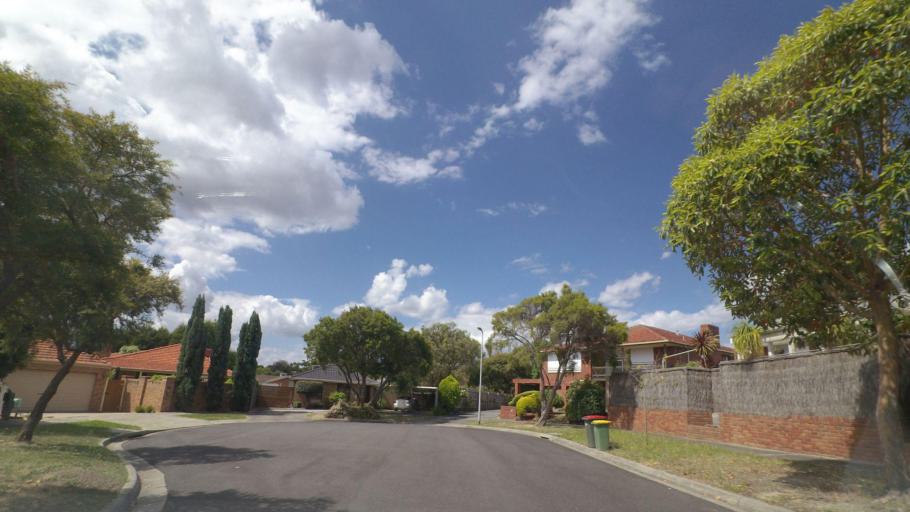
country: AU
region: Victoria
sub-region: Knox
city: Wantirna
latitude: -37.8582
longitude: 145.2210
